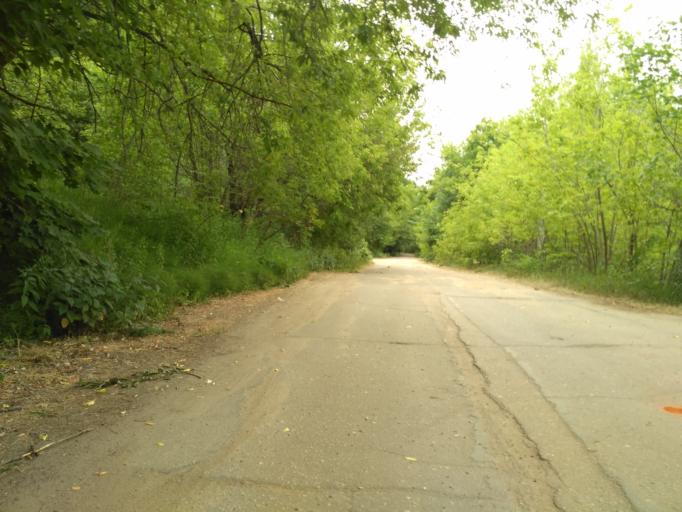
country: RU
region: Nizjnij Novgorod
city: Nizhniy Novgorod
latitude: 56.2926
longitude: 43.9683
